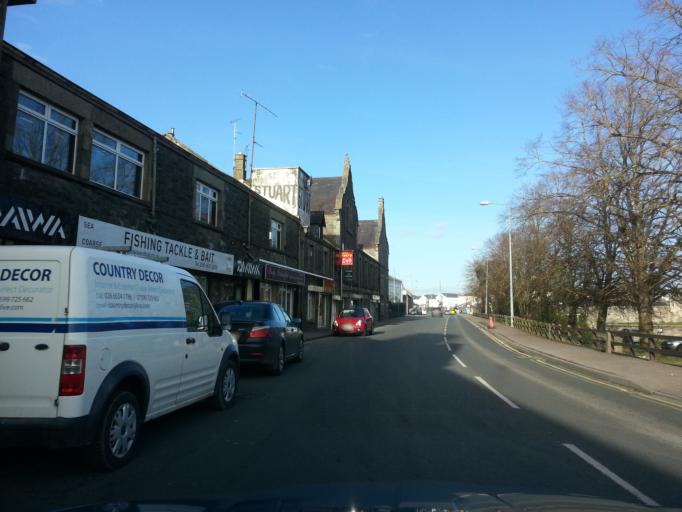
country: GB
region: Northern Ireland
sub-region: Fermanagh District
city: Enniskillen
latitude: 54.3451
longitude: -7.6495
